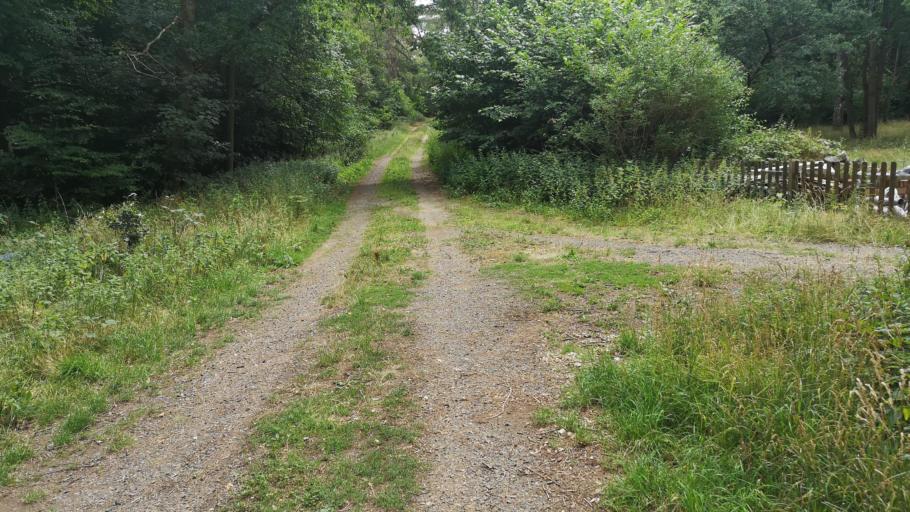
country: DE
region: Lower Saxony
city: Thomasburg
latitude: 53.2393
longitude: 10.7009
